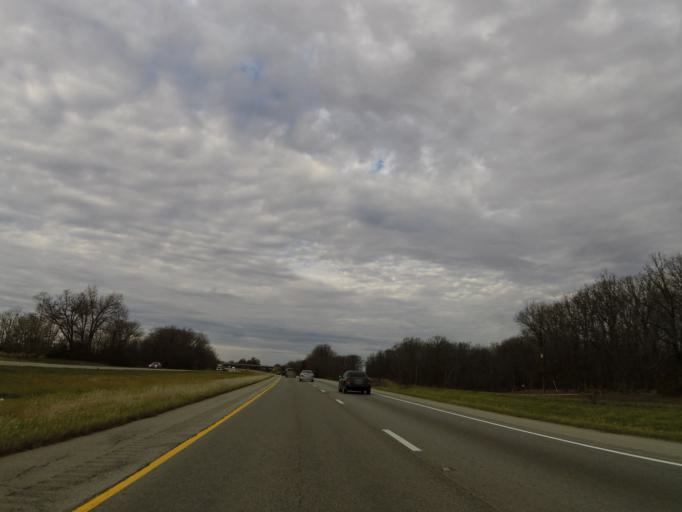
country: US
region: Illinois
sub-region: Clinton County
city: Wamac
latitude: 38.3836
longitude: -89.1208
